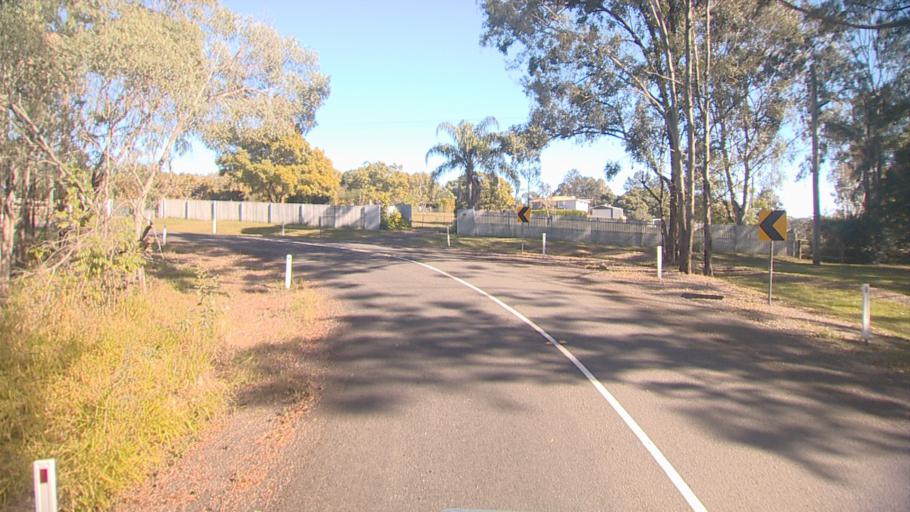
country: AU
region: Queensland
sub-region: Logan
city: Chambers Flat
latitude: -27.7541
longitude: 153.0701
